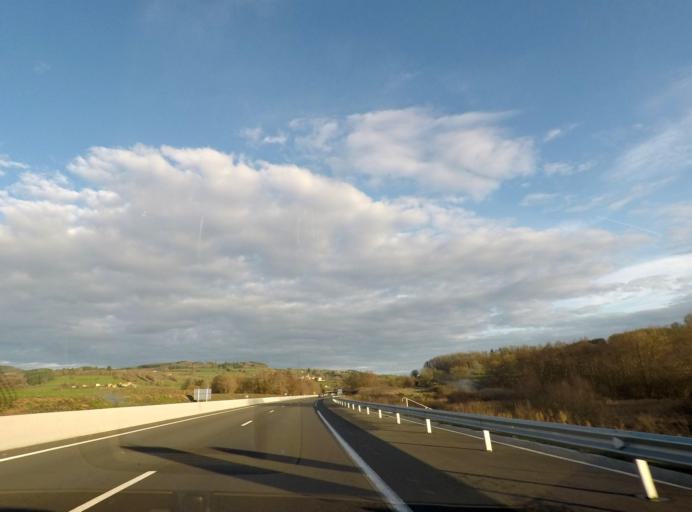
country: FR
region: Bourgogne
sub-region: Departement de Saone-et-Loire
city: Matour
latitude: 46.3807
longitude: 4.5156
